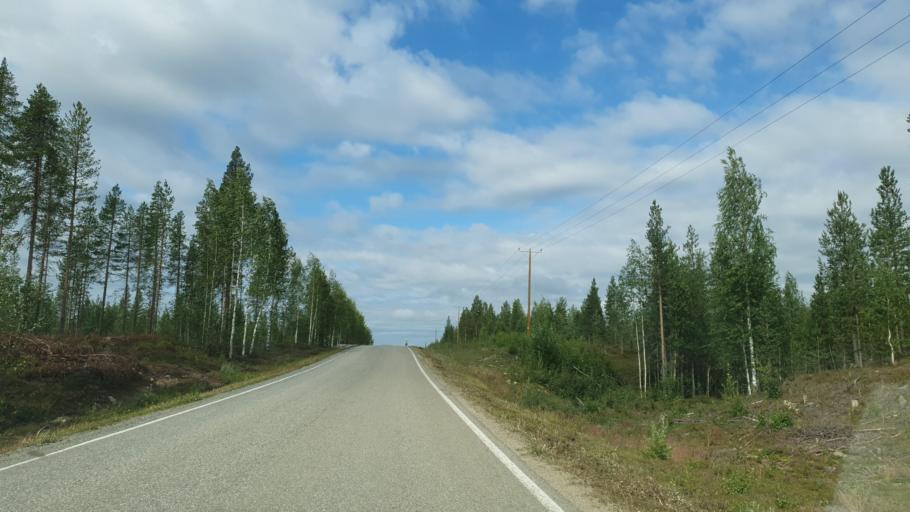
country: FI
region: Lapland
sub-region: Pohjois-Lappi
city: Sodankylae
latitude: 67.5371
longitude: 25.9617
